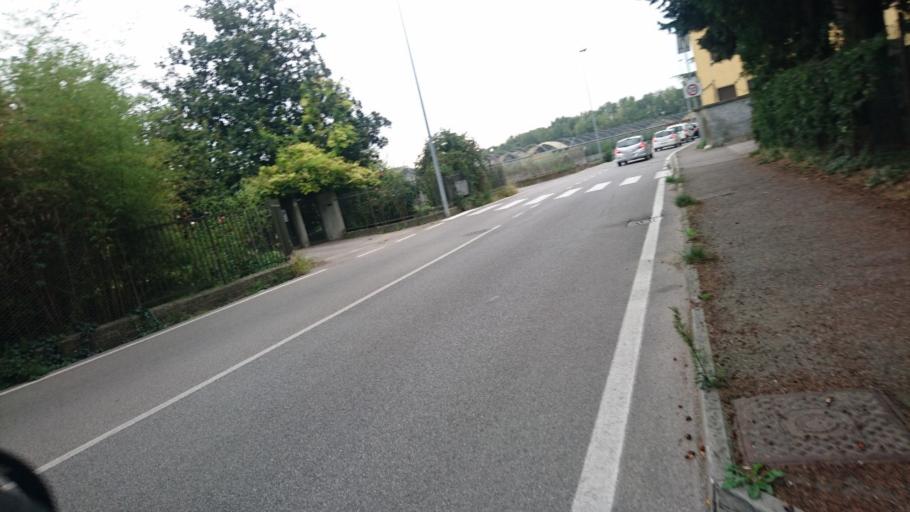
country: IT
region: Veneto
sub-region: Provincia di Verona
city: Verona
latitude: 45.4307
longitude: 11.0212
